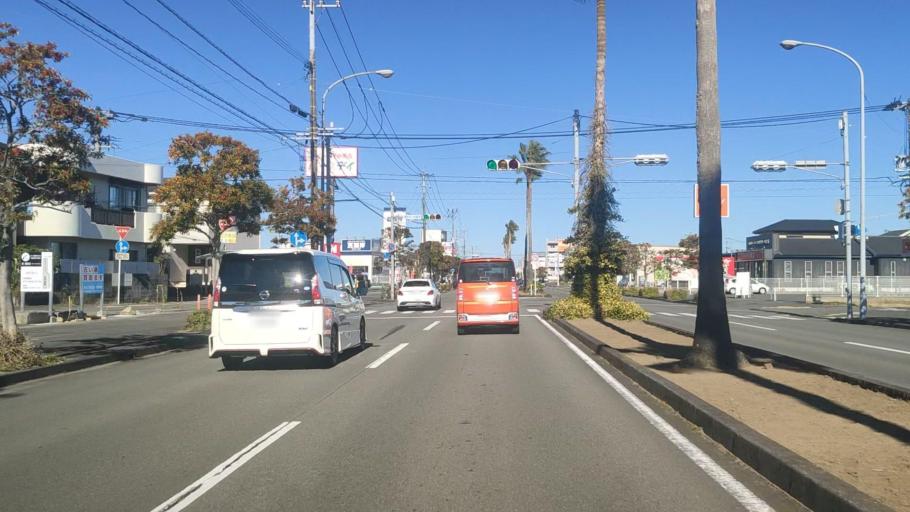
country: JP
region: Miyazaki
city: Miyazaki-shi
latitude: 31.9123
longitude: 131.4478
